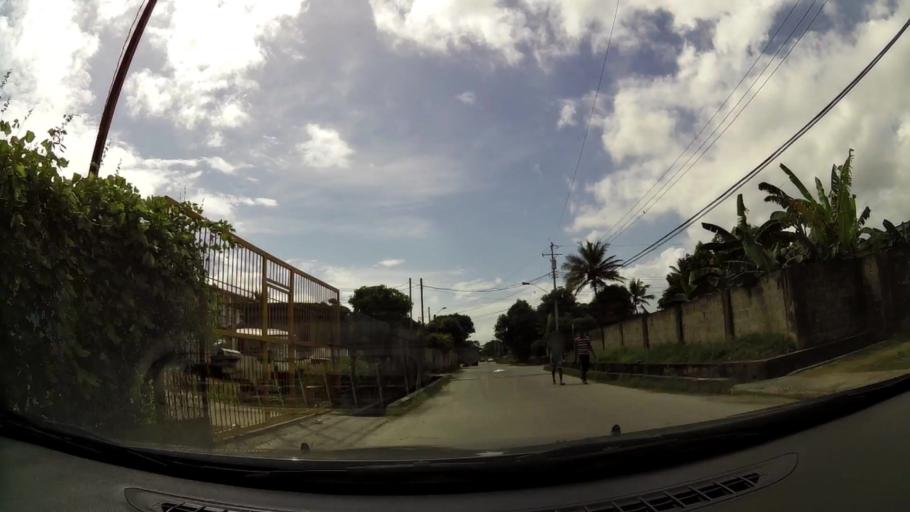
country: TT
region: Borough of Arima
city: Arima
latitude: 10.6282
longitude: -61.2648
